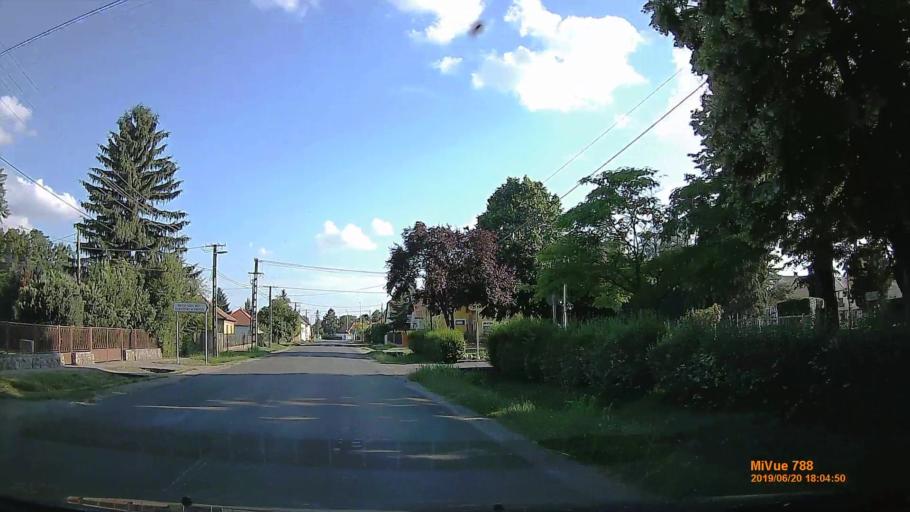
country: HU
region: Baranya
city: Szentlorinc
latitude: 46.0469
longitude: 17.9869
